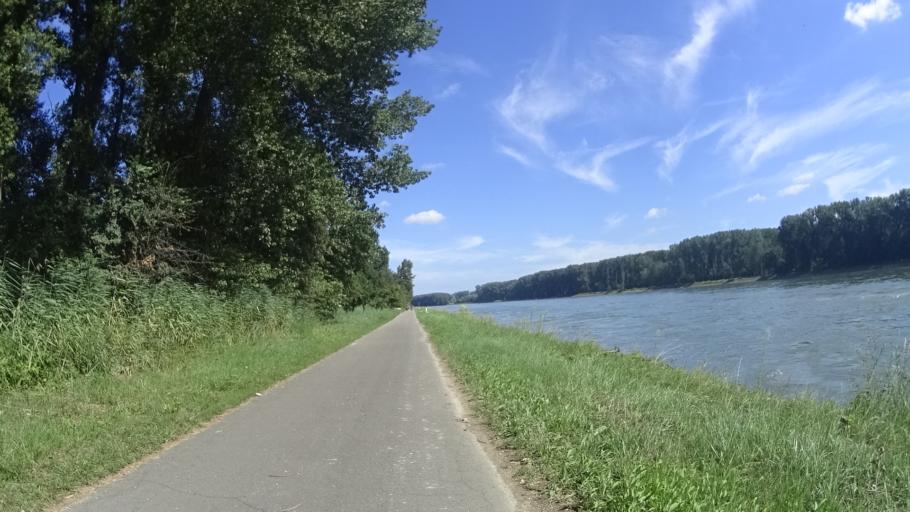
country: DE
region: Rheinland-Pfalz
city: Germersheim
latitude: 49.1993
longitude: 8.3834
